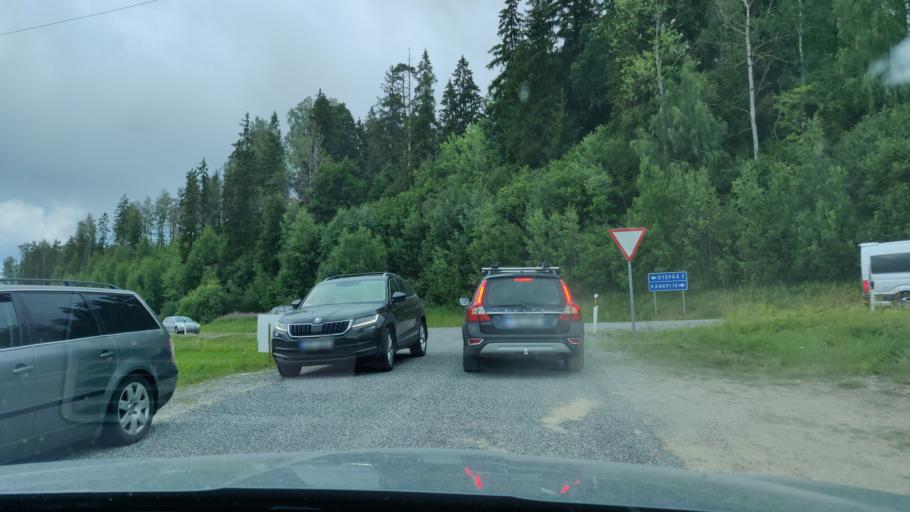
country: EE
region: Vorumaa
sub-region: Antsla vald
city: Vana-Antsla
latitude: 58.0387
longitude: 26.5551
